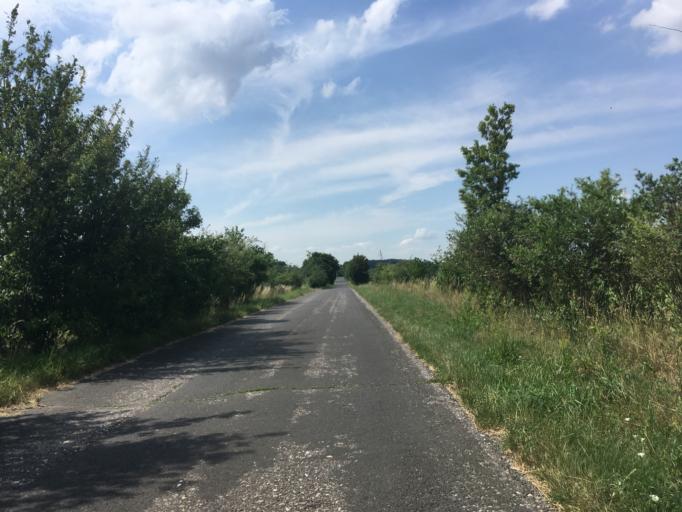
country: DE
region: Saxony-Anhalt
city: Quellendorf
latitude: 51.7814
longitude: 12.1194
